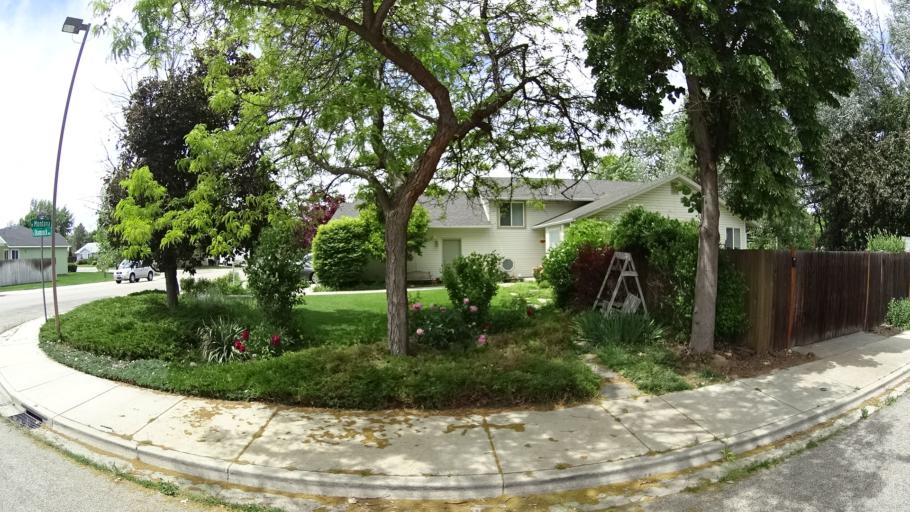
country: US
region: Idaho
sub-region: Ada County
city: Meridian
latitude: 43.6315
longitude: -116.3244
